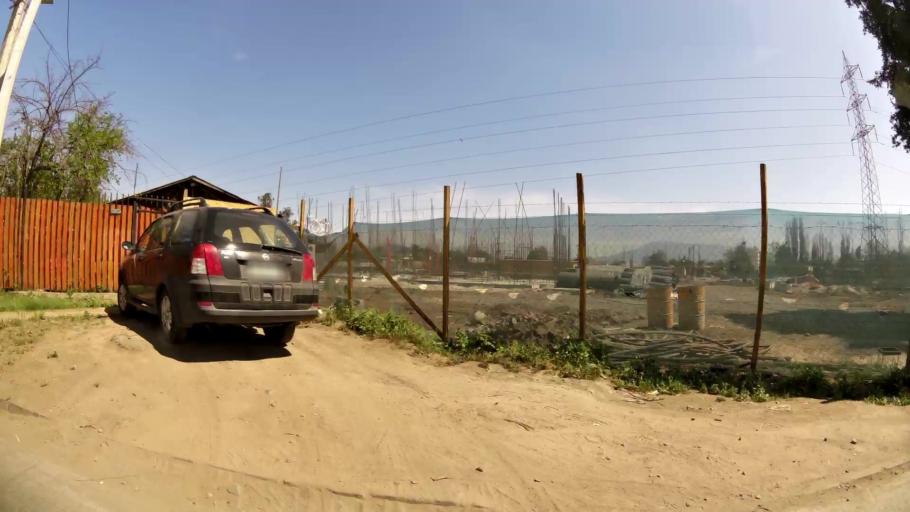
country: CL
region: Santiago Metropolitan
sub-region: Provincia de Santiago
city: Lo Prado
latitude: -33.4039
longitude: -70.7346
